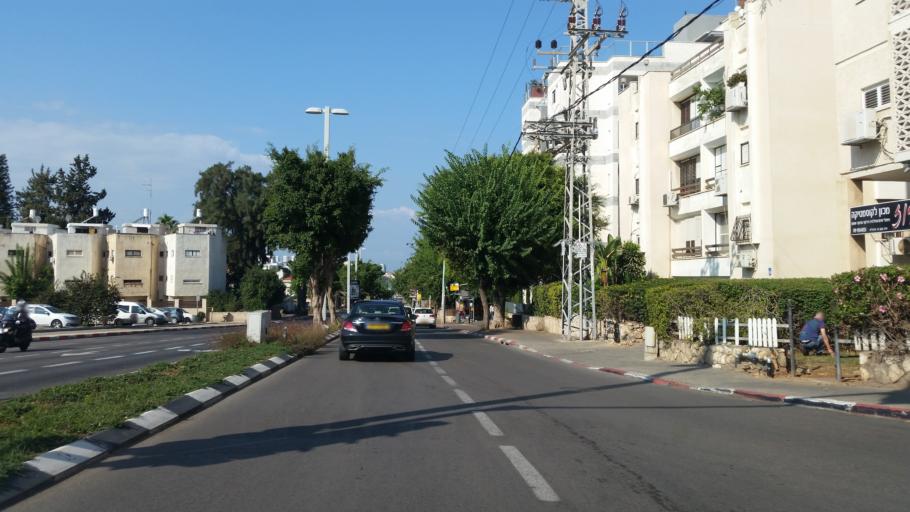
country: IL
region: Tel Aviv
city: Herzliyya
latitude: 32.1624
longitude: 34.8345
